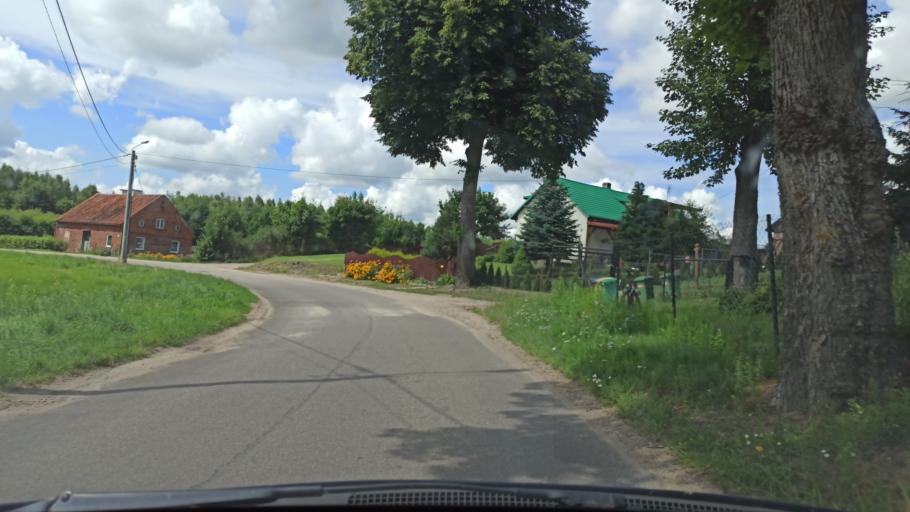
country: PL
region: Warmian-Masurian Voivodeship
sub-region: Powiat ostrodzki
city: Morag
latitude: 53.8674
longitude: 20.0080
